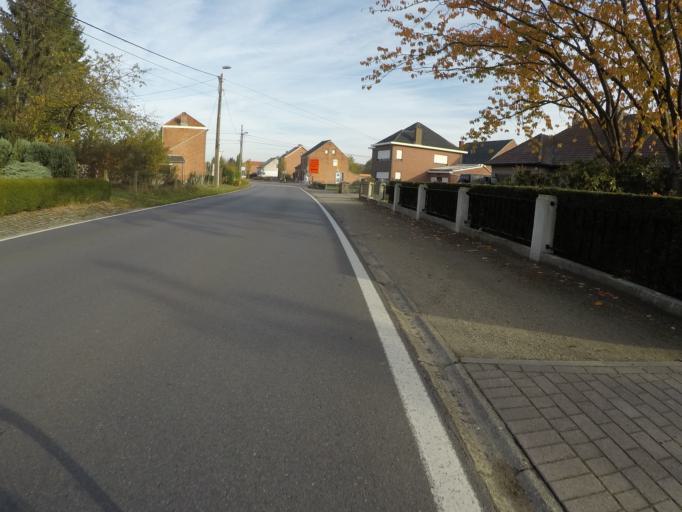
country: BE
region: Flanders
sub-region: Provincie Vlaams-Brabant
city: Begijnendijk
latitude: 50.9878
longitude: 4.7539
